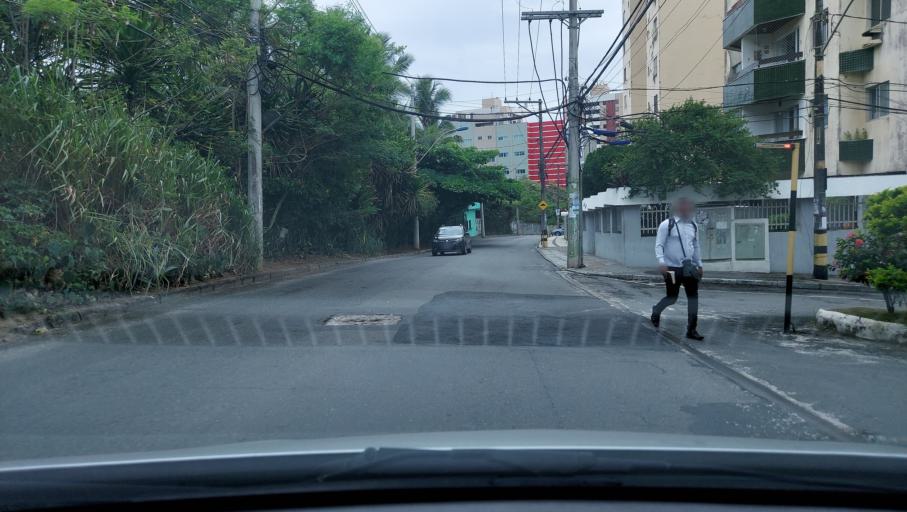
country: BR
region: Bahia
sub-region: Salvador
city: Salvador
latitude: -12.9875
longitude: -38.4442
